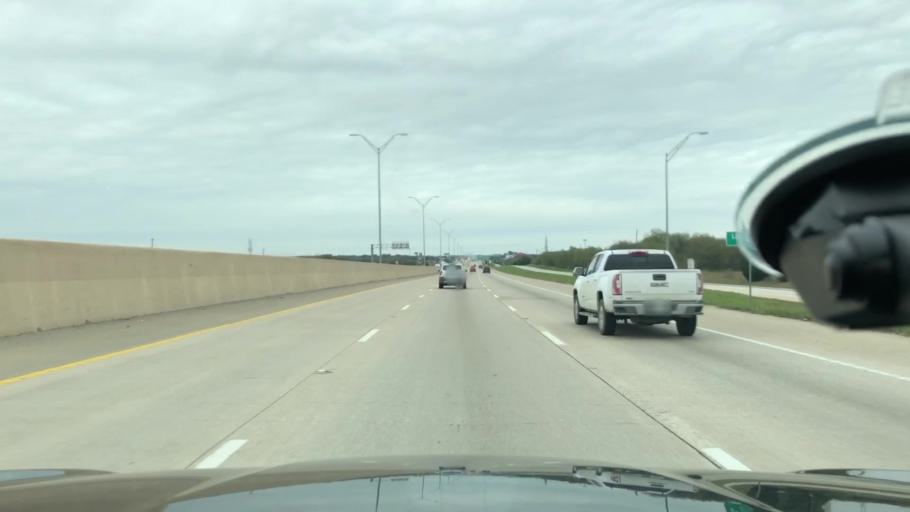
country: US
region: Texas
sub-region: Dallas County
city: Glenn Heights
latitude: 32.5498
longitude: -96.8223
